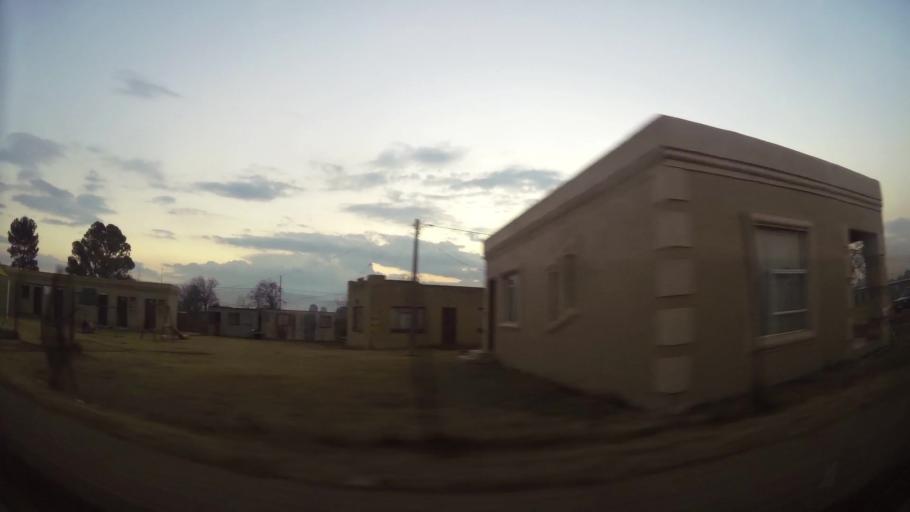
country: ZA
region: Gauteng
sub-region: City of Johannesburg Metropolitan Municipality
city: Orange Farm
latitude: -26.5391
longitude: 27.8450
